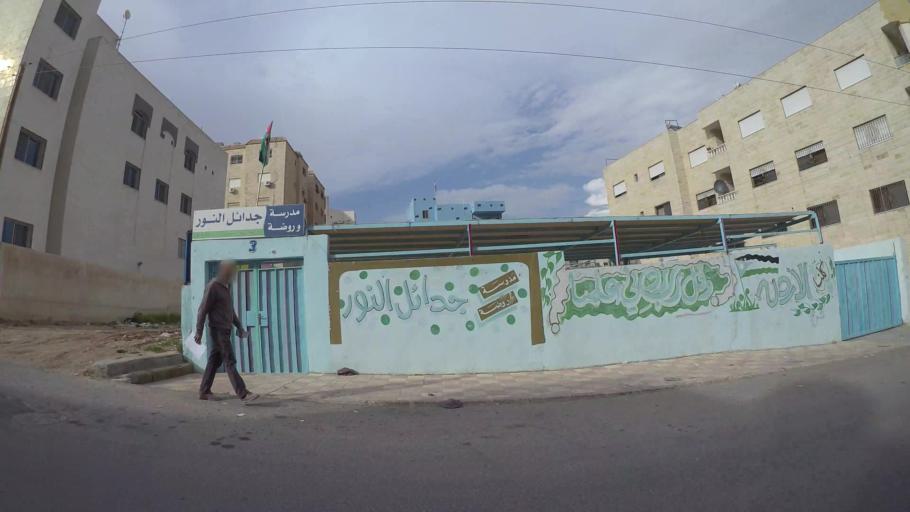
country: JO
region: Amman
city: Amman
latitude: 32.0027
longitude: 35.9426
